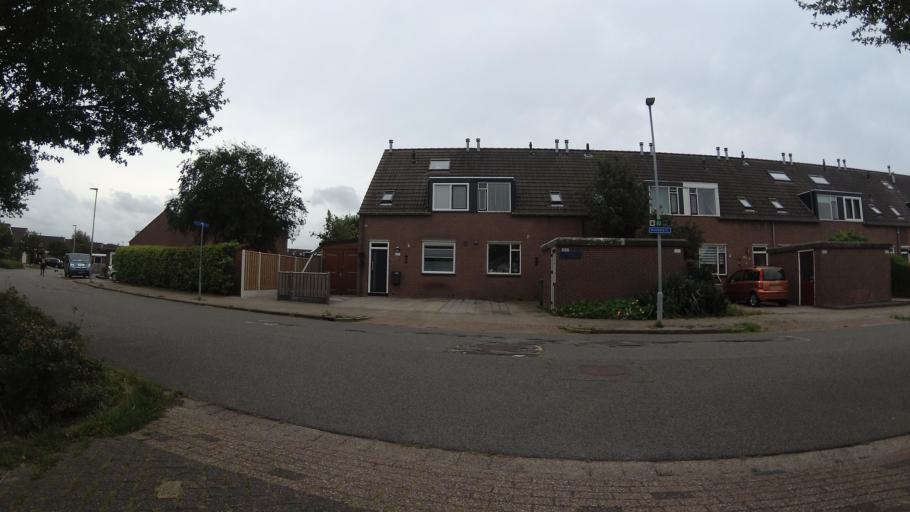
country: NL
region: North Holland
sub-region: Gemeente Den Helder
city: Den Helder
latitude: 52.8902
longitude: 4.7353
